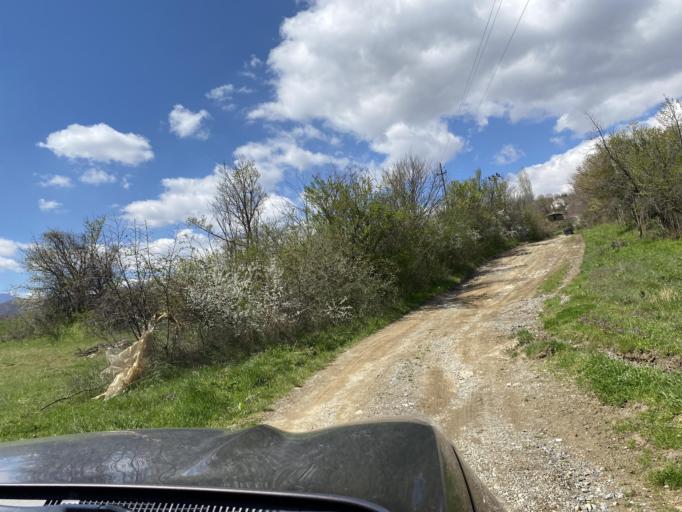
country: MK
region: Caska
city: Caska
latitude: 41.7352
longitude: 21.6446
